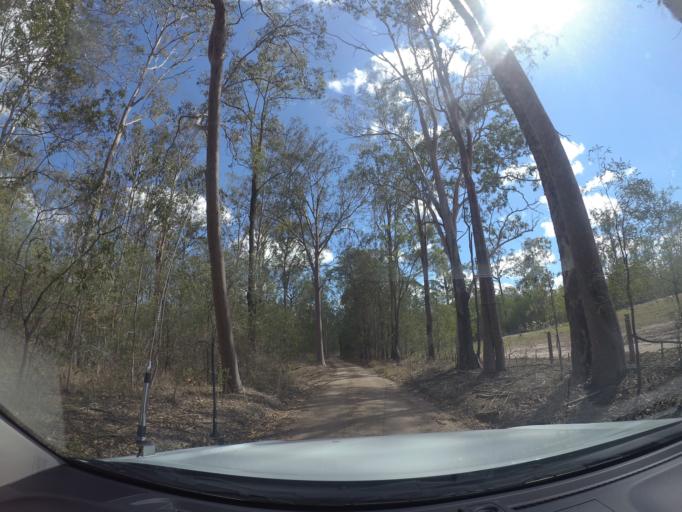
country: AU
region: Queensland
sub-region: Logan
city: North Maclean
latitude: -27.8235
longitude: 152.9689
